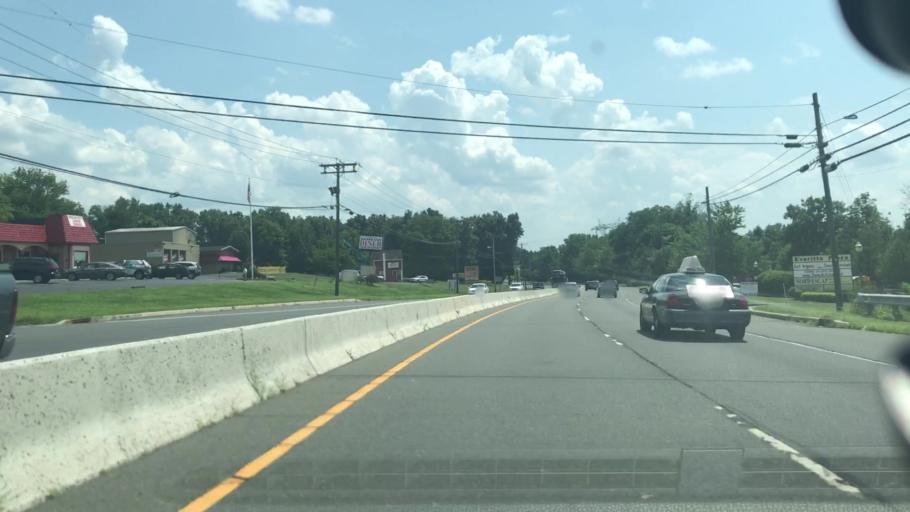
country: US
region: New Jersey
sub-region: Hunterdon County
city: Flemington
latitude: 40.4598
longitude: -74.8593
